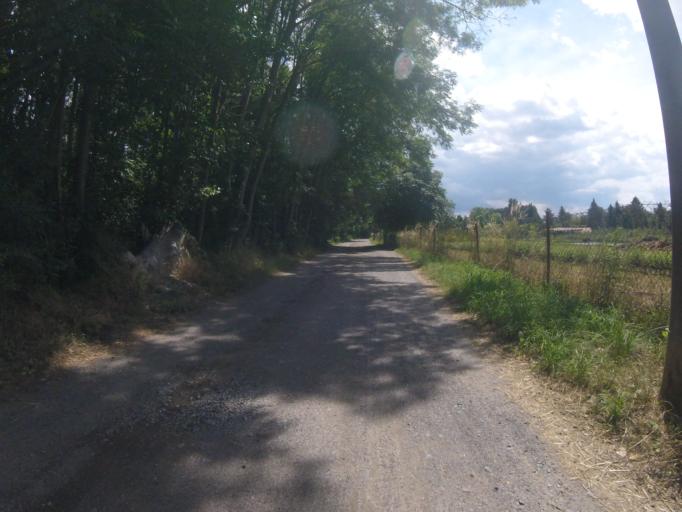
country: DE
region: Brandenburg
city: Bestensee
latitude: 52.2665
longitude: 13.6427
